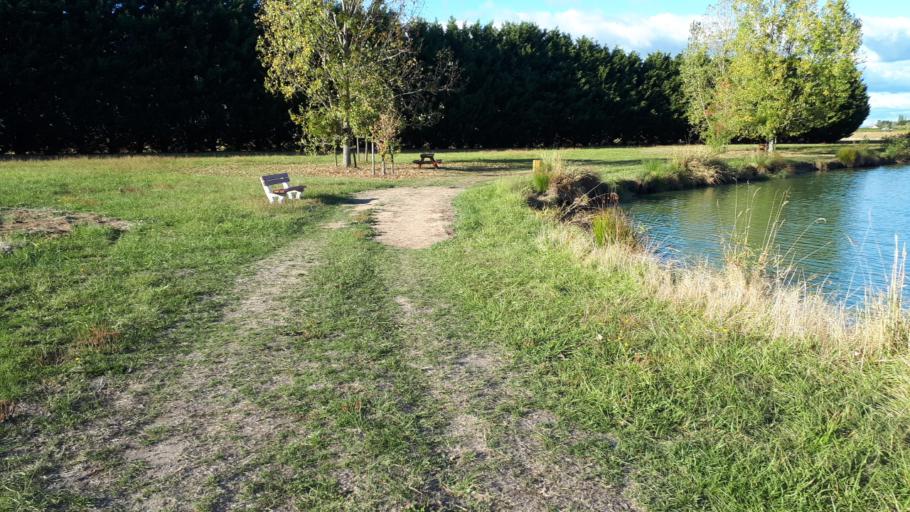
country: FR
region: Centre
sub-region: Departement du Loir-et-Cher
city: Saint-Romain-sur-Cher
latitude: 47.3650
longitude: 1.3979
